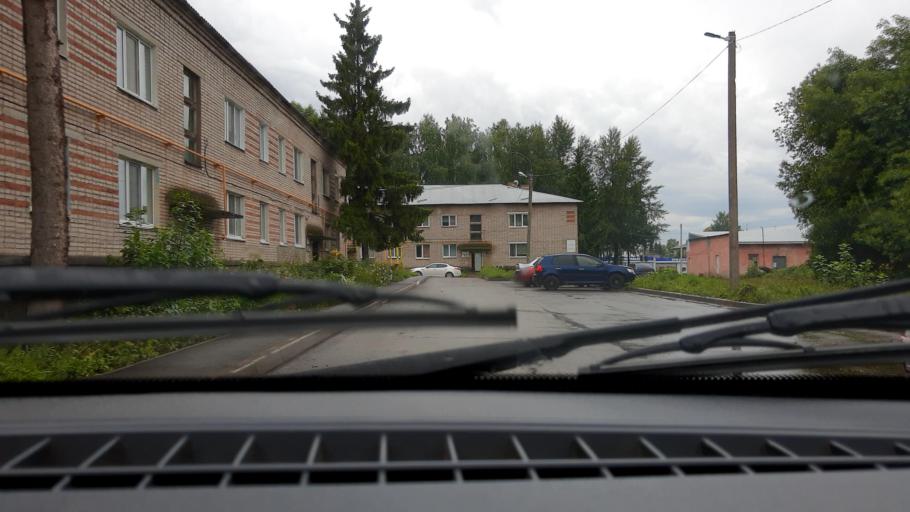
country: RU
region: Bashkortostan
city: Avdon
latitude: 54.8197
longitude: 55.6977
